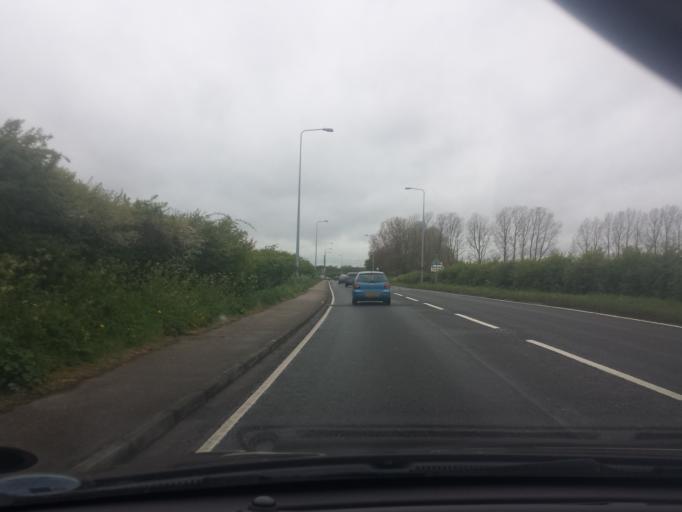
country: GB
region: England
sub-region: Essex
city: Great Bentley
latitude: 51.8596
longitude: 1.1065
